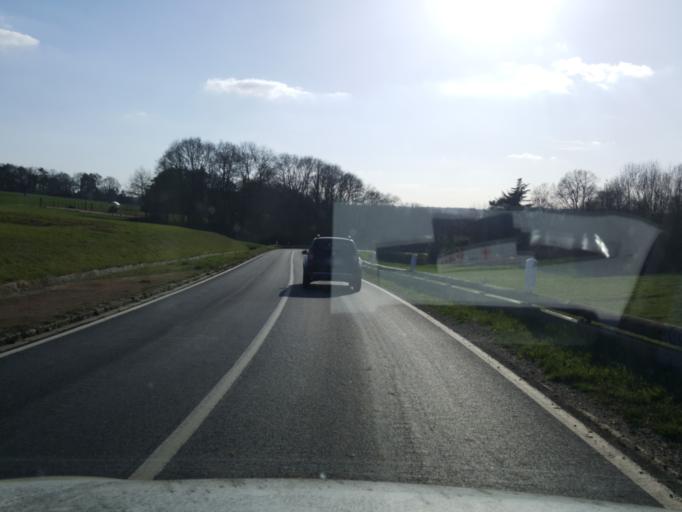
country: FR
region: Centre
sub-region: Departement d'Eure-et-Loir
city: Epernon
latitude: 48.6512
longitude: 1.7015
